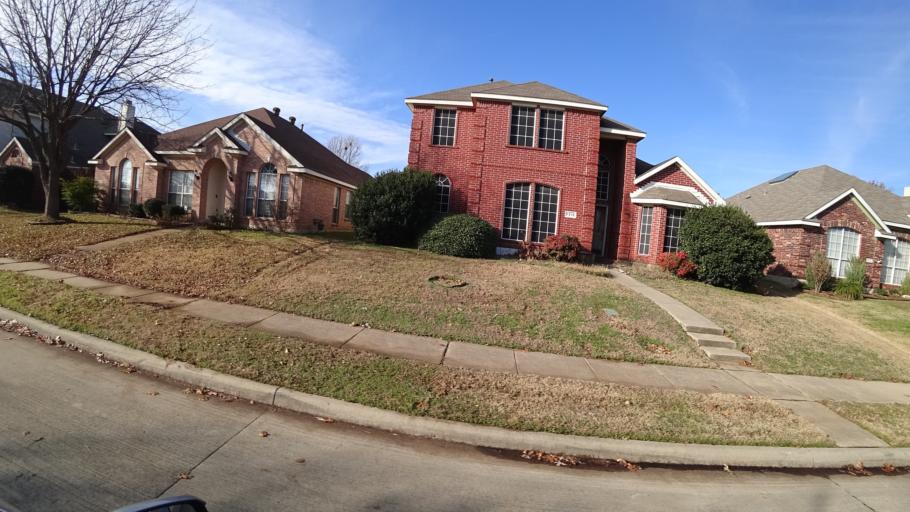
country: US
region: Texas
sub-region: Denton County
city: Lewisville
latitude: 33.0612
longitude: -97.0216
